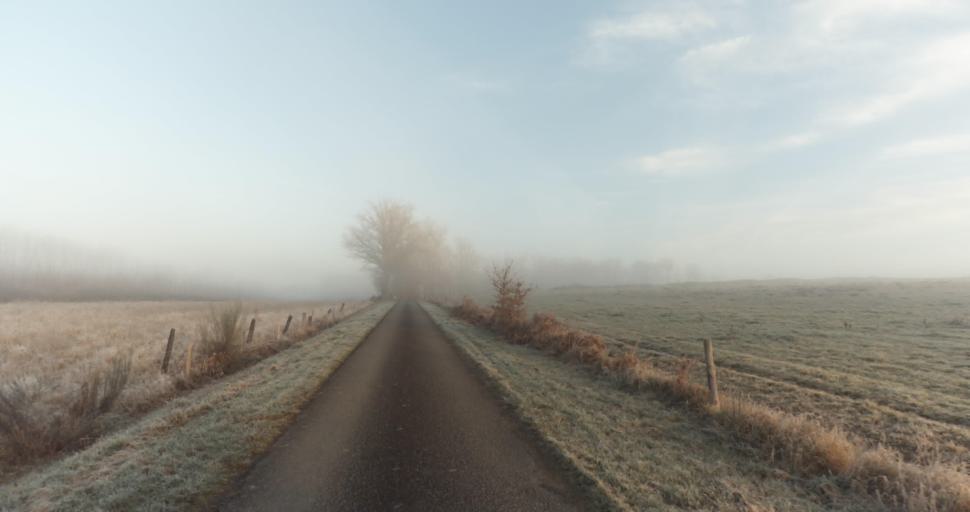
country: FR
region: Limousin
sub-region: Departement de la Haute-Vienne
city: Saint-Priest-sous-Aixe
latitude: 45.8226
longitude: 1.1222
